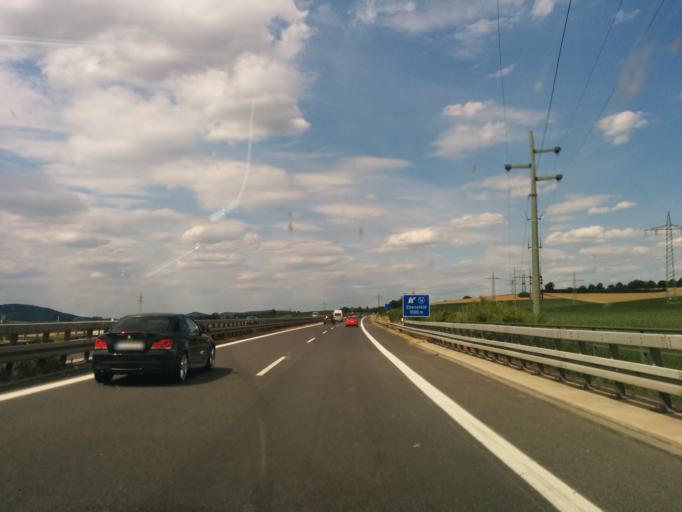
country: DE
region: Bavaria
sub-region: Upper Franconia
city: Ebensfeld
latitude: 50.0493
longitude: 10.9602
